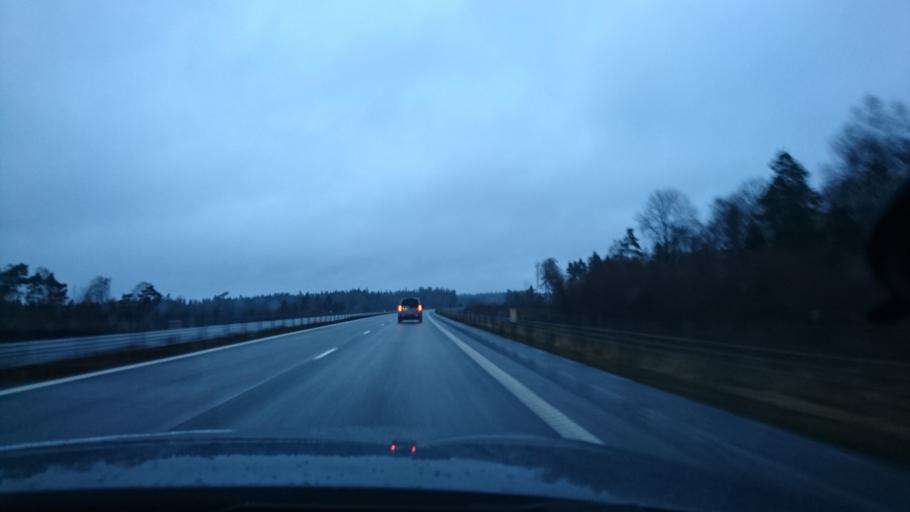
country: SE
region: Kronoberg
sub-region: Markaryds Kommun
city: Markaryd
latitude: 56.3786
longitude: 13.5047
